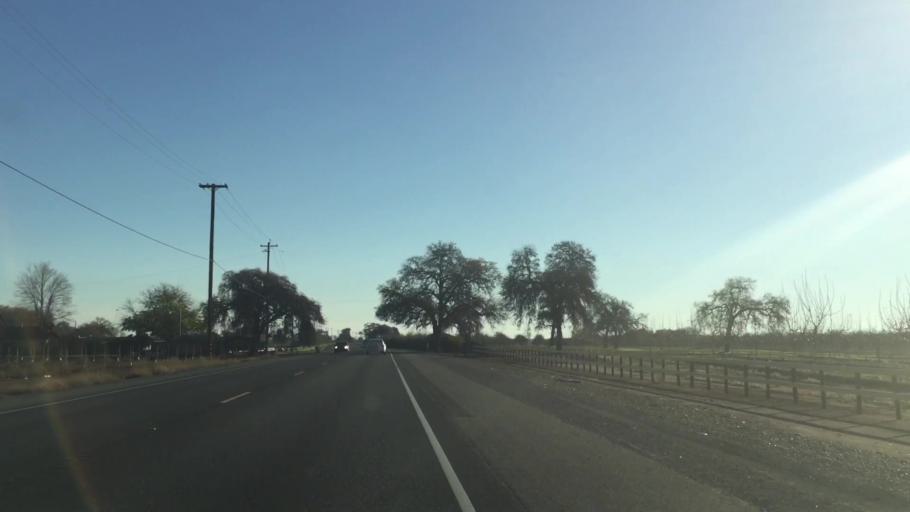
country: US
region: California
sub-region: Sutter County
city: Live Oak
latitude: 39.3438
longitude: -121.6001
